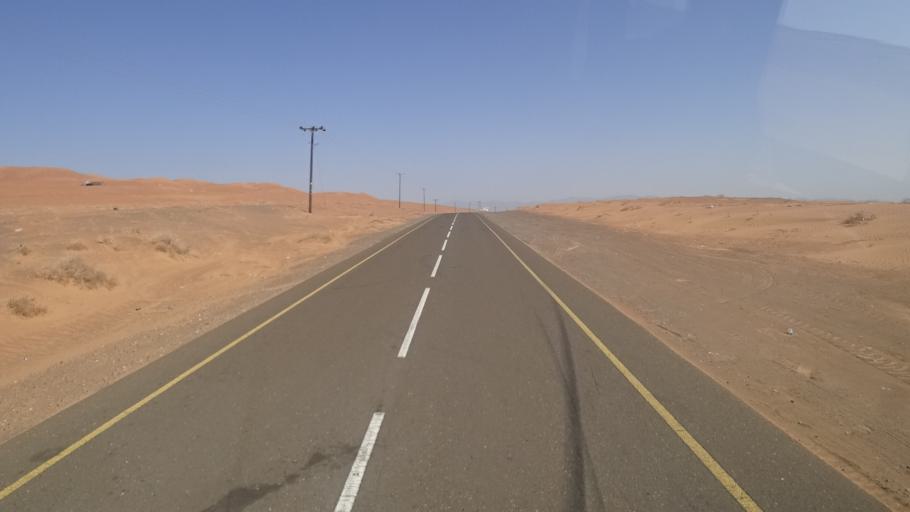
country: OM
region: Ash Sharqiyah
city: Al Qabil
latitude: 22.4922
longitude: 58.7152
